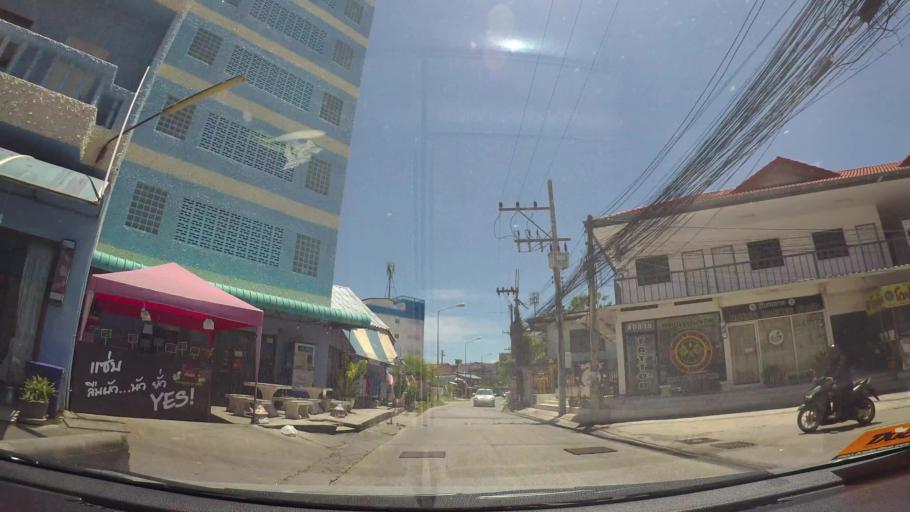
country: TH
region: Chon Buri
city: Phatthaya
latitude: 12.9251
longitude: 100.8908
